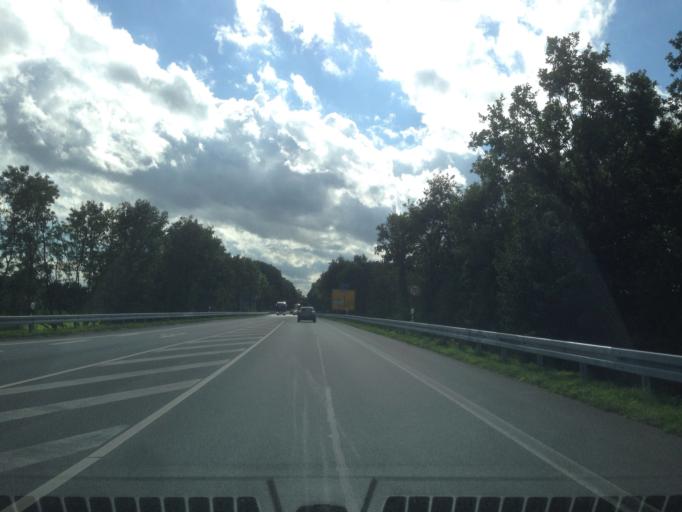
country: DE
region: North Rhine-Westphalia
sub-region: Regierungsbezirk Munster
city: Muenster
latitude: 51.9908
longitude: 7.5418
